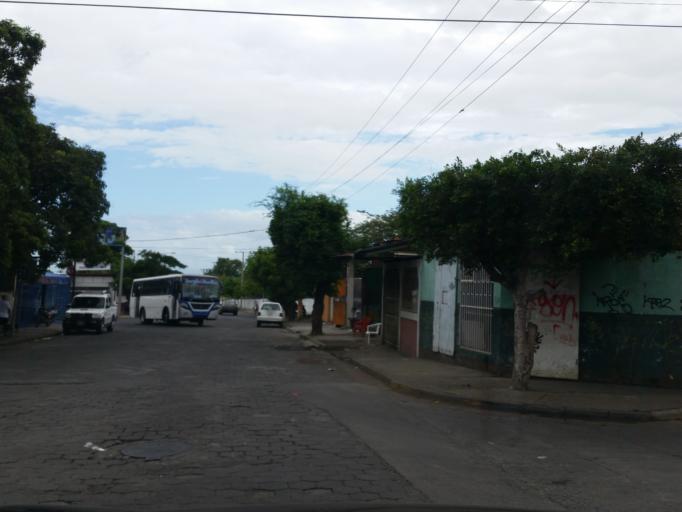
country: NI
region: Managua
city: Managua
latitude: 12.1374
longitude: -86.2382
